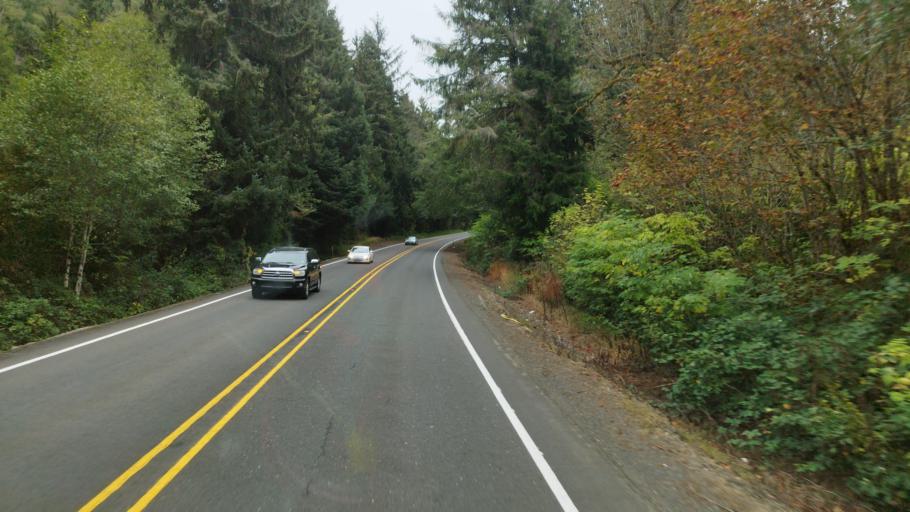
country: US
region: Oregon
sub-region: Clatsop County
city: Cannon Beach
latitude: 45.9027
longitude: -123.8583
